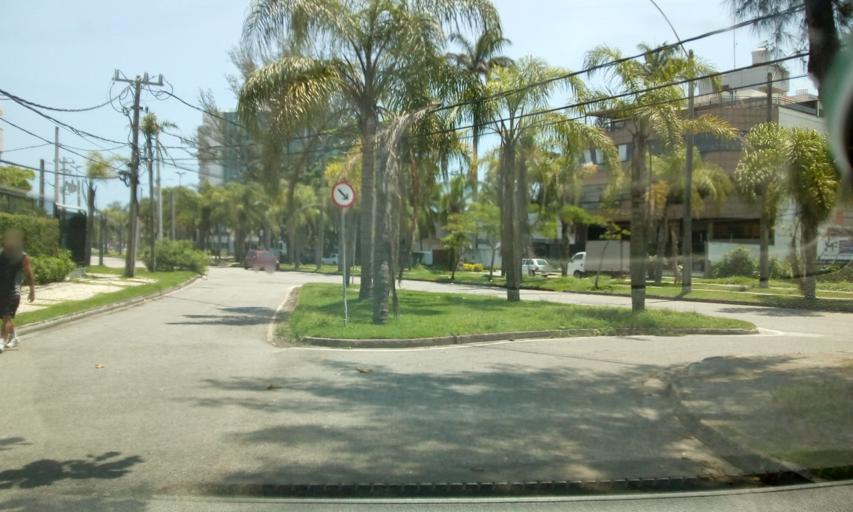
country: BR
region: Rio de Janeiro
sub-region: Nilopolis
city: Nilopolis
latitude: -23.0288
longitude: -43.4689
